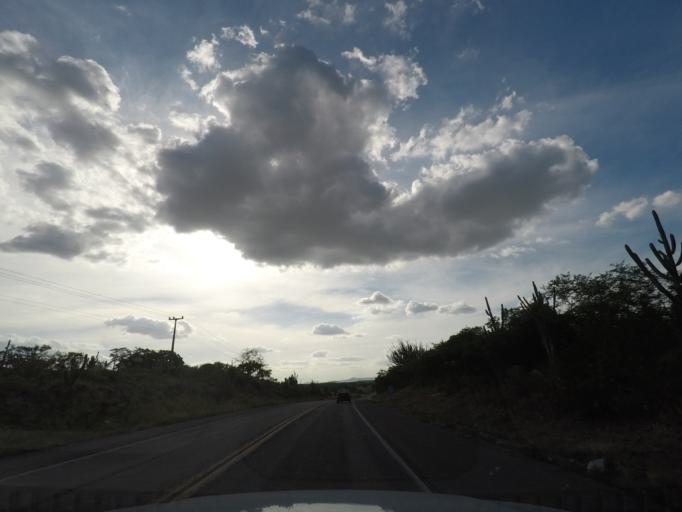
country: BR
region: Bahia
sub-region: Anguera
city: Anguera
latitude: -12.1869
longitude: -39.4885
